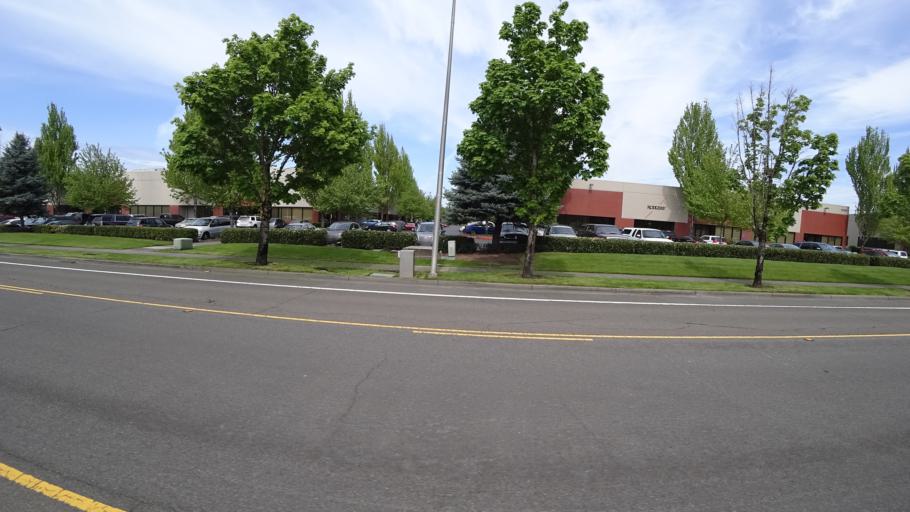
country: US
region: Oregon
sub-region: Washington County
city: Rockcreek
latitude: 45.5646
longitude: -122.8978
